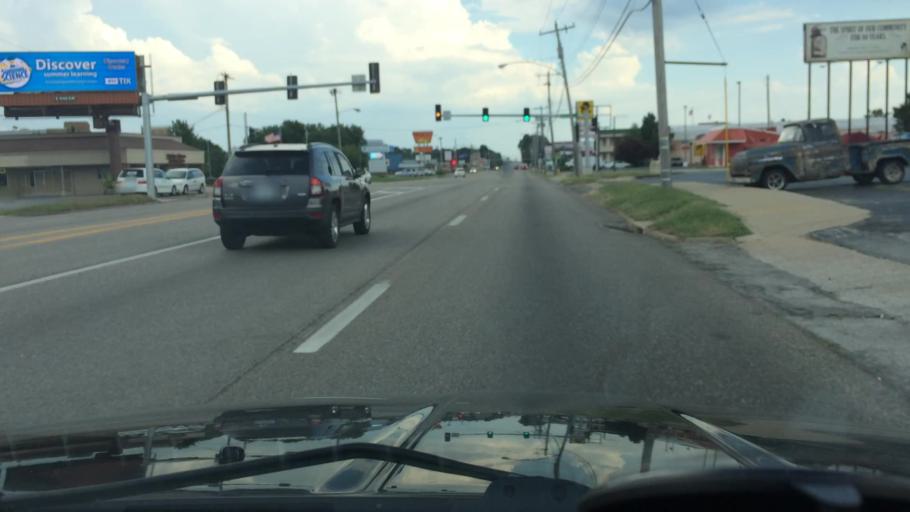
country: US
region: Missouri
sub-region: Greene County
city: Springfield
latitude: 37.1789
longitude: -93.2625
